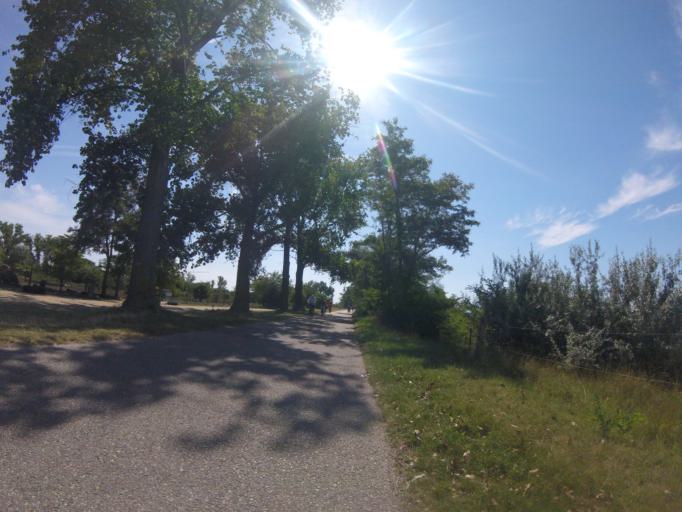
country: AT
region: Burgenland
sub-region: Politischer Bezirk Neusiedl am See
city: Podersdorf am See
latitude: 47.8324
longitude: 16.8063
